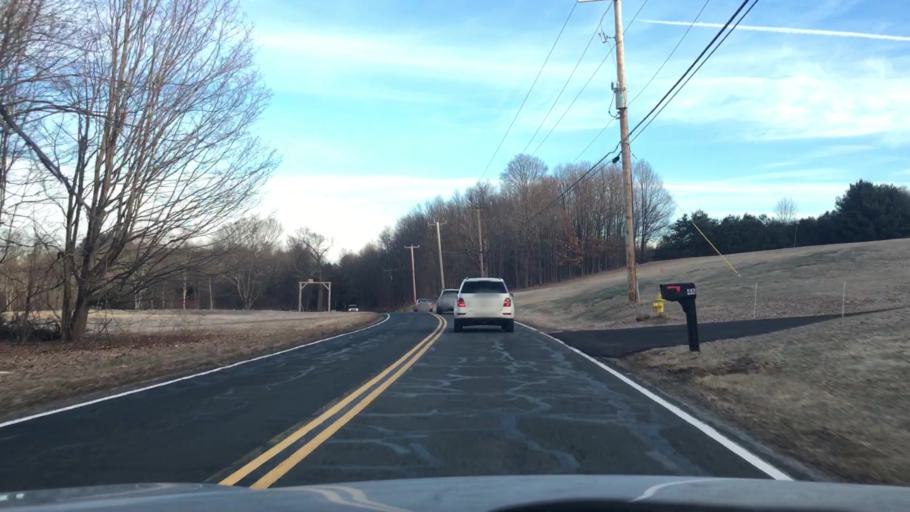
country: US
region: Massachusetts
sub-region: Hampden County
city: Southwick
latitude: 42.0696
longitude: -72.7233
